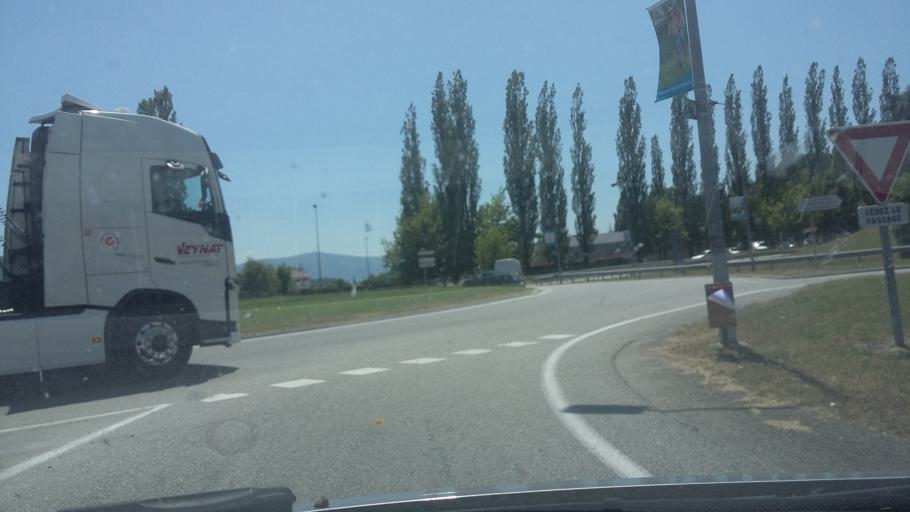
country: FR
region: Rhone-Alpes
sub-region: Departement de l'Ain
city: Belley
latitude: 45.7588
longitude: 5.7052
